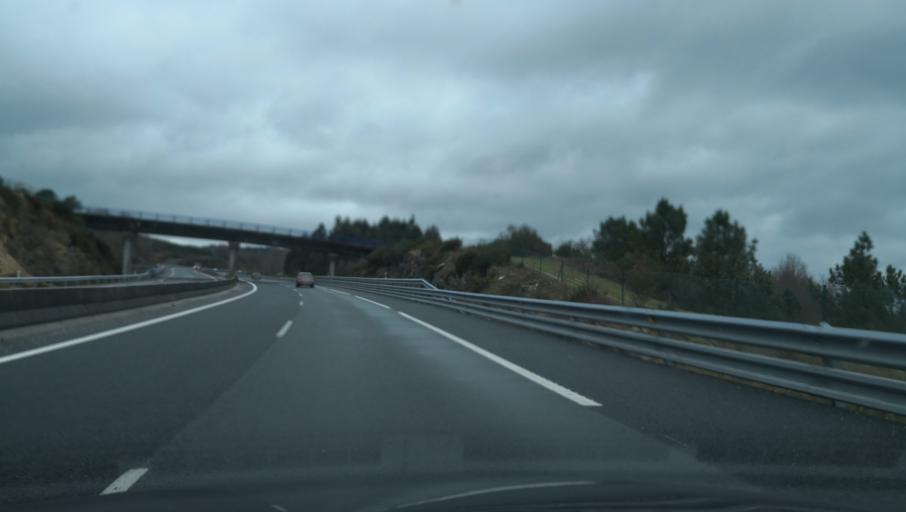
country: ES
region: Galicia
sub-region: Provincia de Ourense
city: Pinor
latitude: 42.5378
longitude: -8.0157
